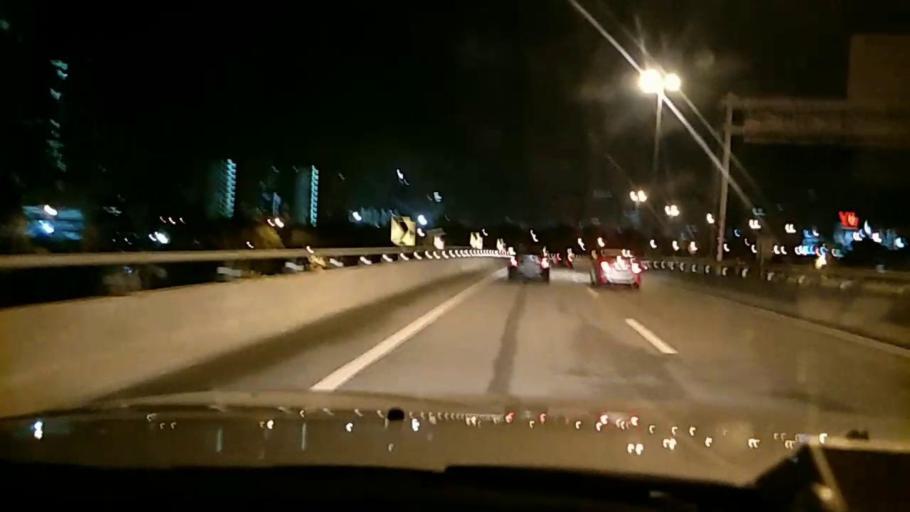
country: MY
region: Kuala Lumpur
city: Kuala Lumpur
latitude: 3.1294
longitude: 101.7187
